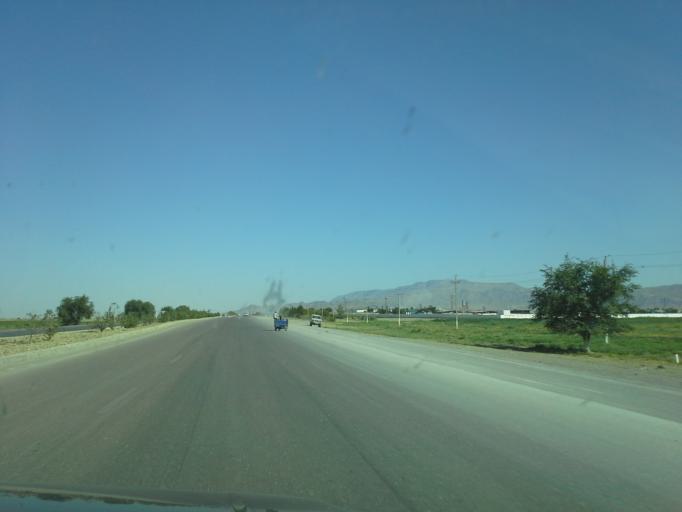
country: TM
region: Ahal
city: Baharly
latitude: 38.3269
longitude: 57.5859
